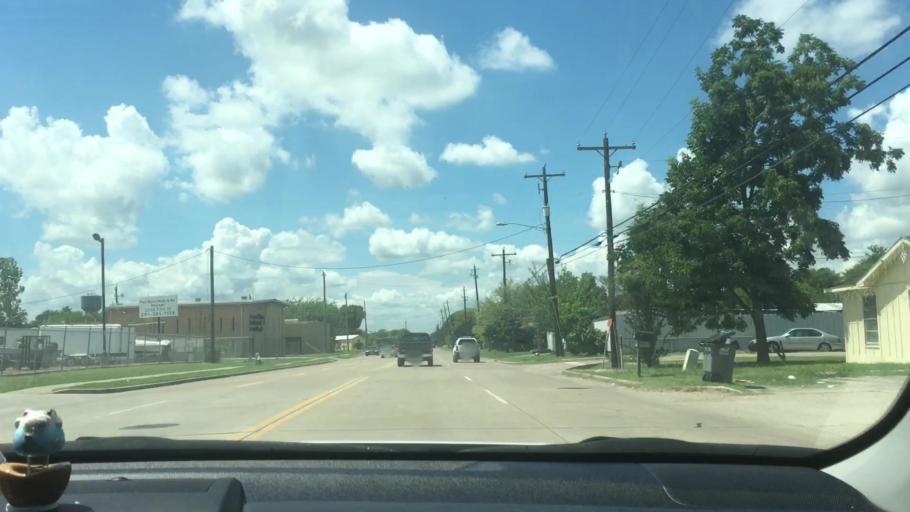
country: US
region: Texas
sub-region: Fort Bend County
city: Fifth Street
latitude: 29.5966
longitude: -95.5579
